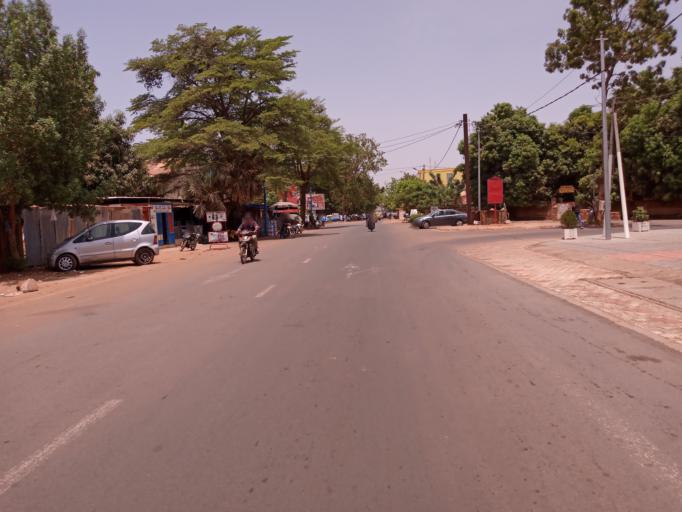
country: ML
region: Bamako
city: Bamako
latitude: 12.6339
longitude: -8.0000
